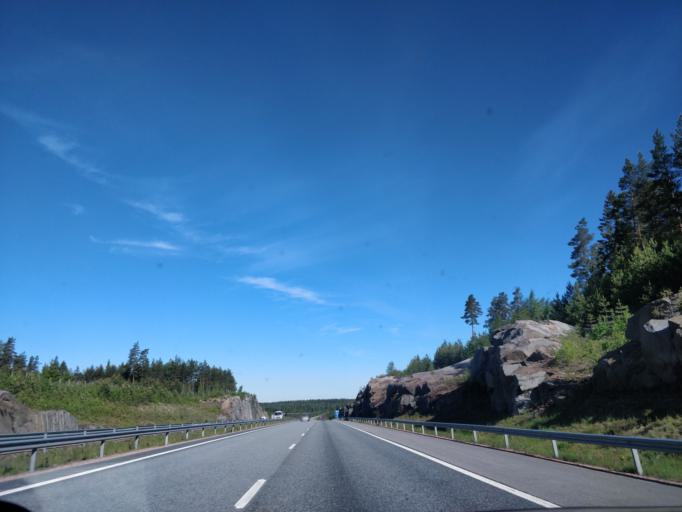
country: FI
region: Varsinais-Suomi
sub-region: Salo
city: Suomusjaervi
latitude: 60.3752
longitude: 23.6404
